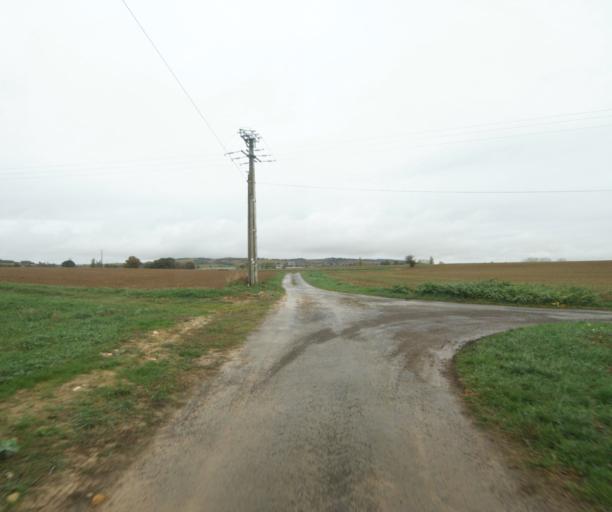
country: FR
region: Rhone-Alpes
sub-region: Departement de l'Ain
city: Pont-de-Vaux
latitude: 46.4854
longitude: 4.8796
